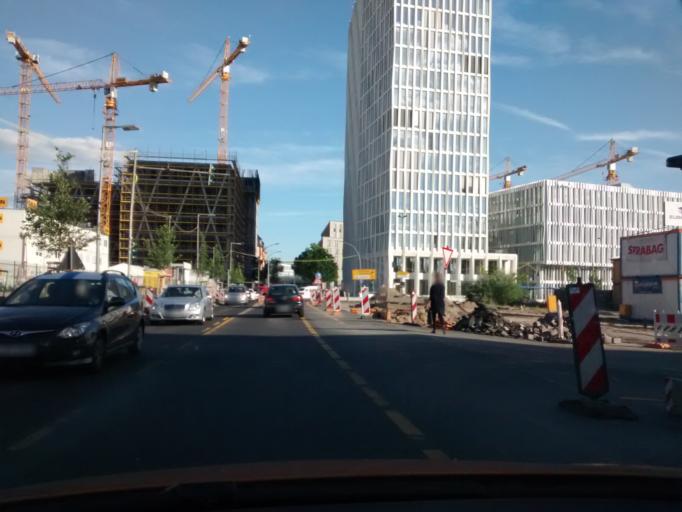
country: DE
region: Berlin
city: Tiergarten Bezirk
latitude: 52.5296
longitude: 13.3693
